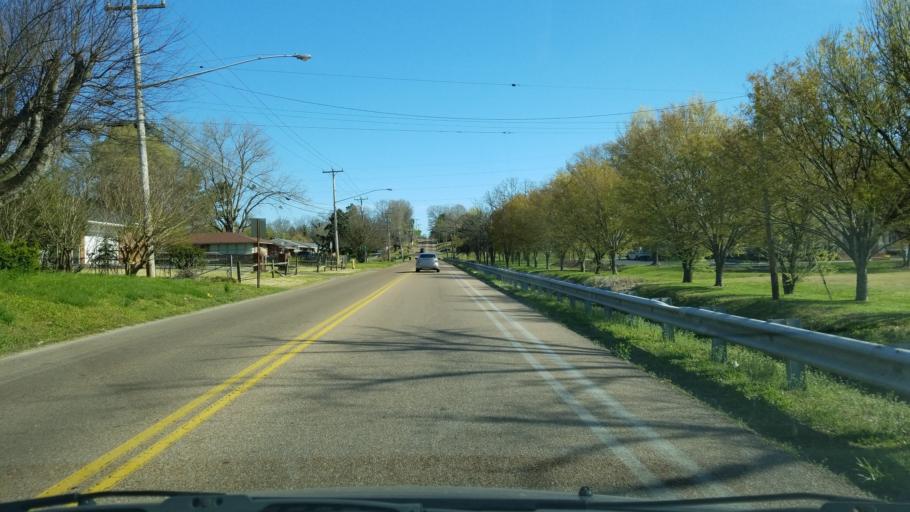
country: US
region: Tennessee
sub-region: Hamilton County
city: Harrison
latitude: 35.0790
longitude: -85.1874
